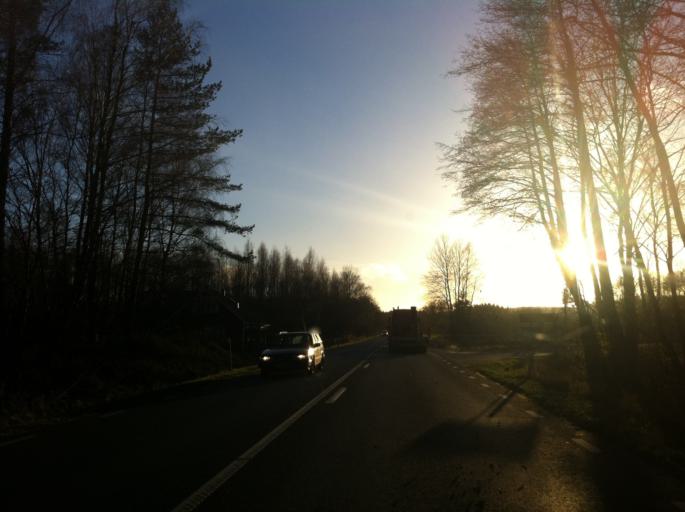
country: SE
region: Skane
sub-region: Hassleholms Kommun
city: Hassleholm
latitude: 56.1775
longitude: 13.8420
